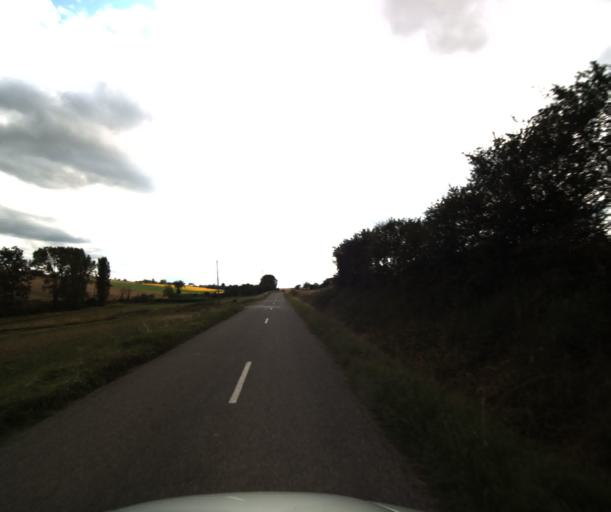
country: FR
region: Midi-Pyrenees
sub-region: Departement de la Haute-Garonne
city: Eaunes
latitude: 43.4105
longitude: 1.3293
